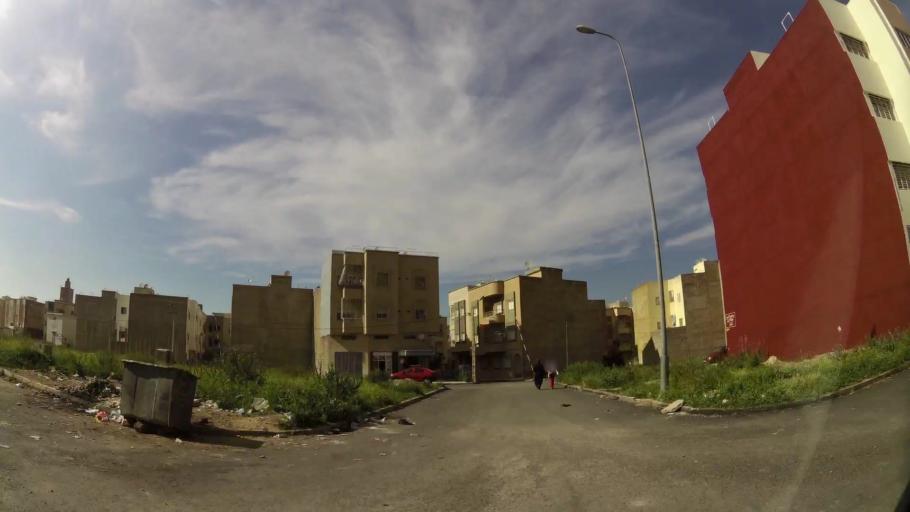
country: MA
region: Fes-Boulemane
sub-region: Fes
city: Fes
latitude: 34.0120
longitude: -5.0363
